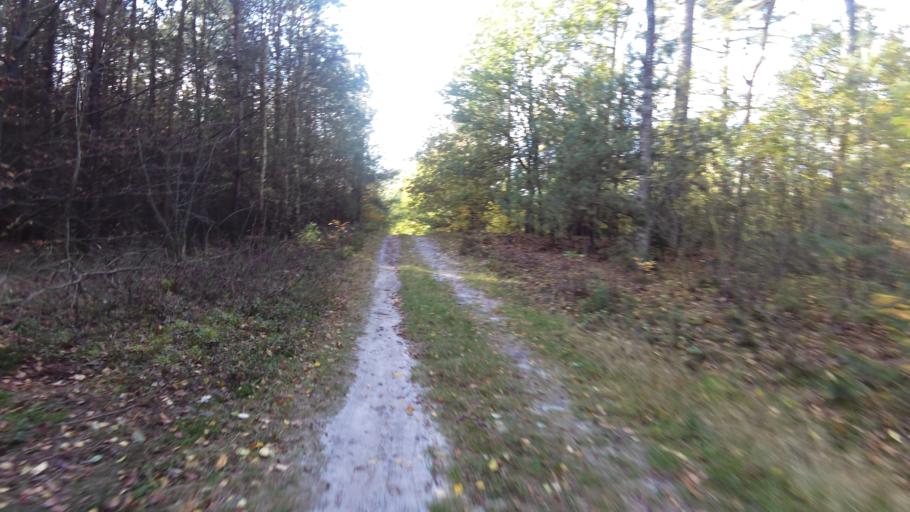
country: NL
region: Gelderland
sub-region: Gemeente Hattem
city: Hattem
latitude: 52.4364
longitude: 6.0440
